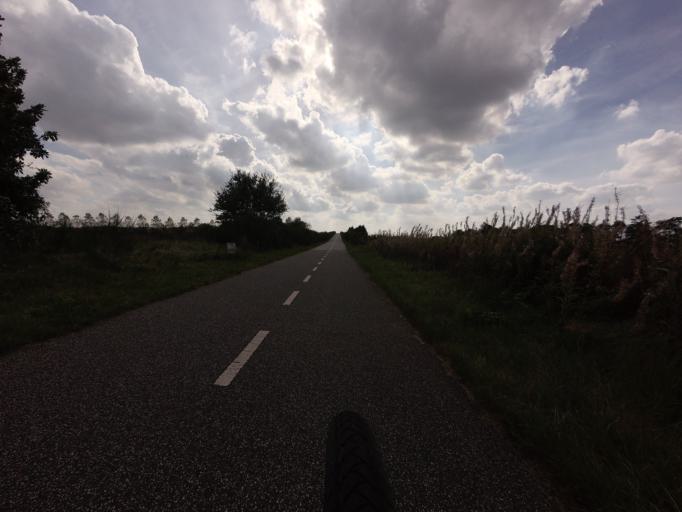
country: DK
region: Central Jutland
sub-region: Herning Kommune
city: Sunds
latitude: 56.1916
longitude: 9.0122
